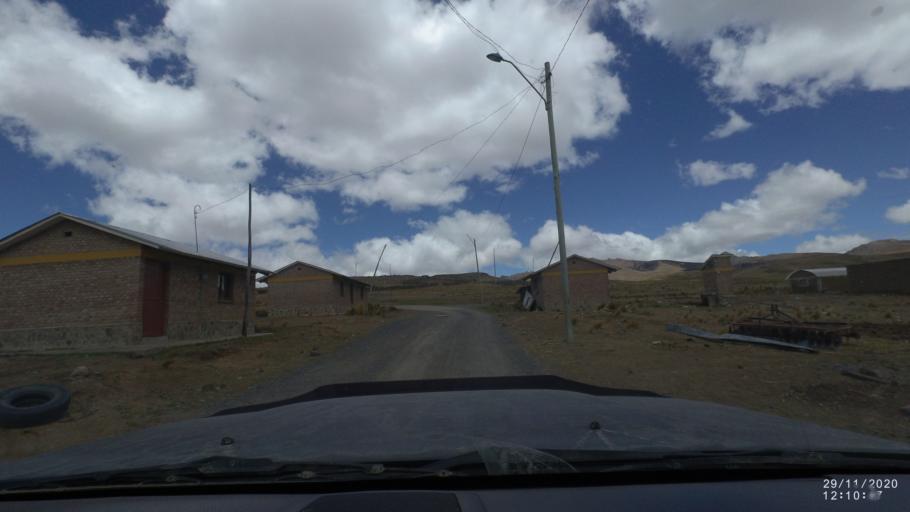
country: BO
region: Cochabamba
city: Cochabamba
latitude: -17.1231
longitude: -66.3058
